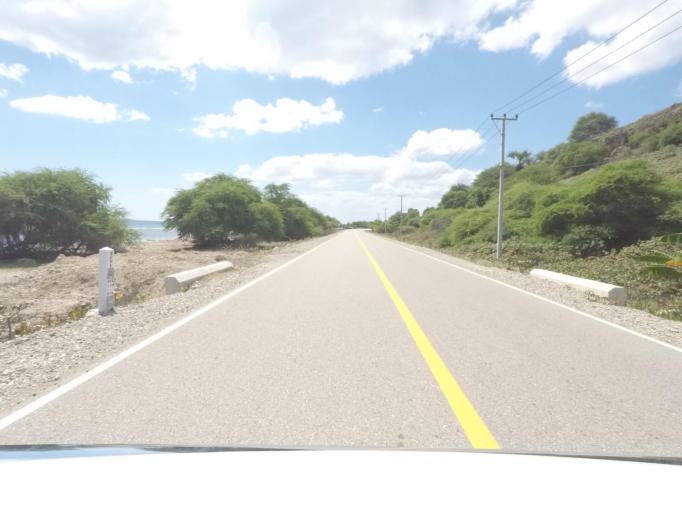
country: TL
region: Baucau
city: Baucau
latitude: -8.4090
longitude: 126.7222
